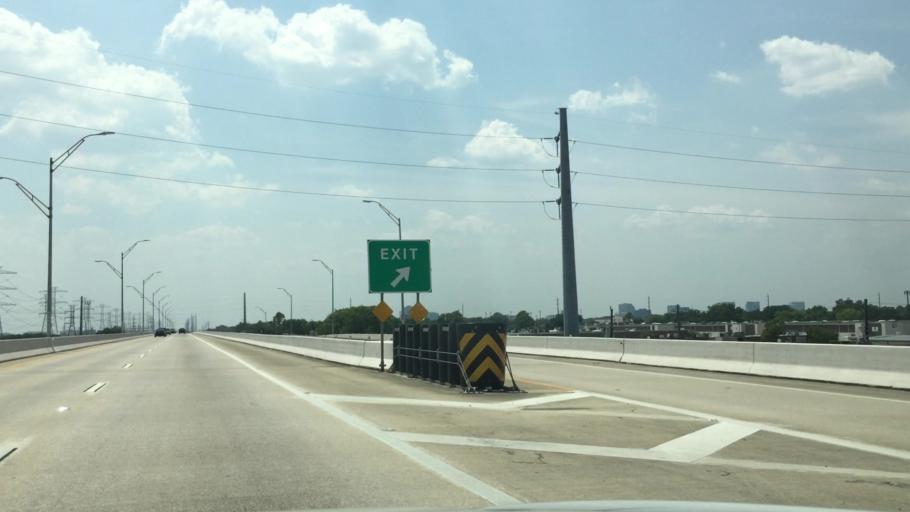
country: US
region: Texas
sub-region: Harris County
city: Piney Point Village
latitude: 29.7219
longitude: -95.5128
